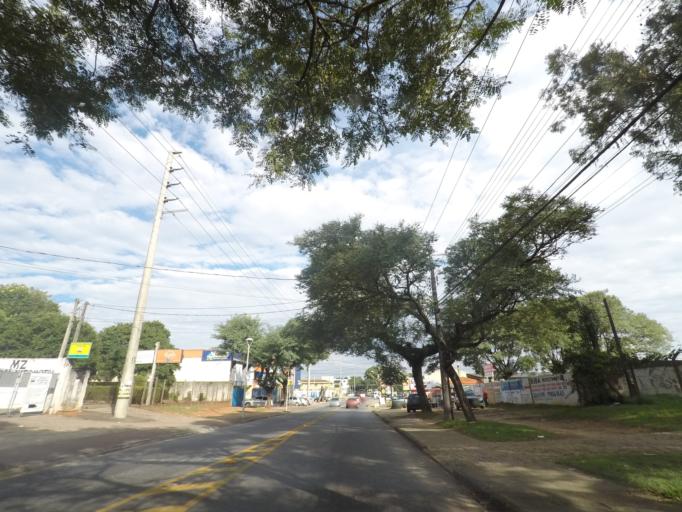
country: BR
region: Parana
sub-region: Sao Jose Dos Pinhais
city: Sao Jose dos Pinhais
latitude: -25.5382
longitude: -49.2948
